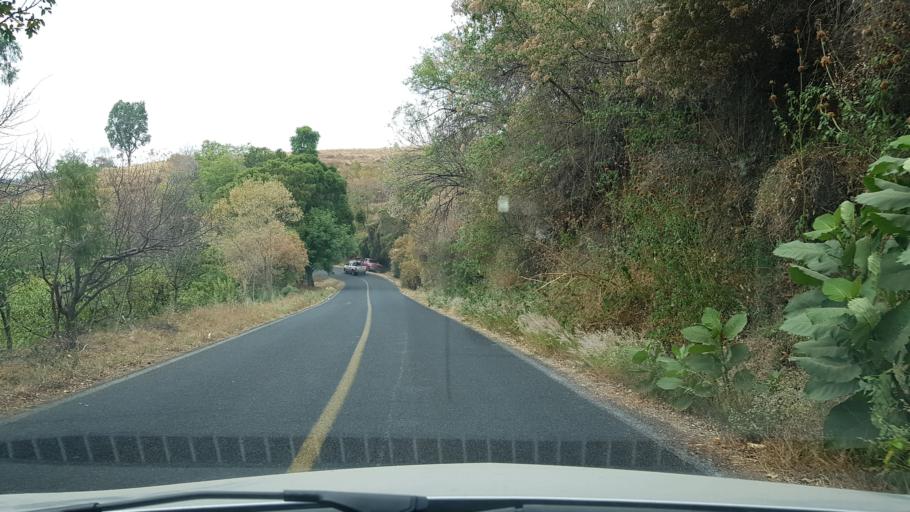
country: MX
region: Morelos
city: Tlacotepec
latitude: 18.8357
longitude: -98.7249
